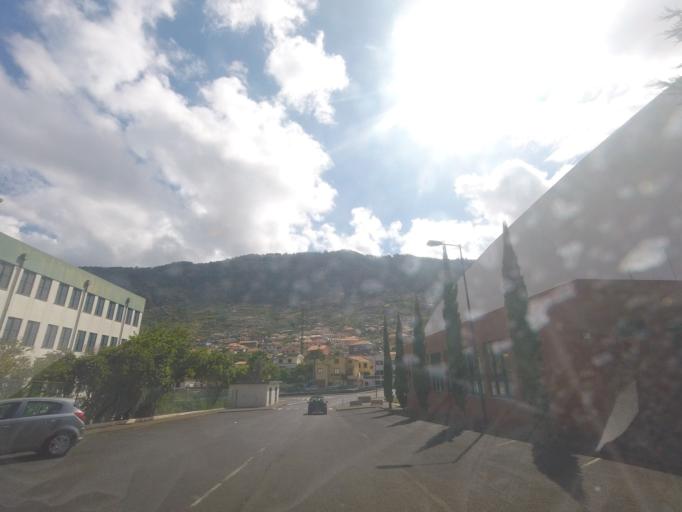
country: PT
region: Madeira
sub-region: Machico
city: Machico
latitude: 32.7263
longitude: -16.7711
